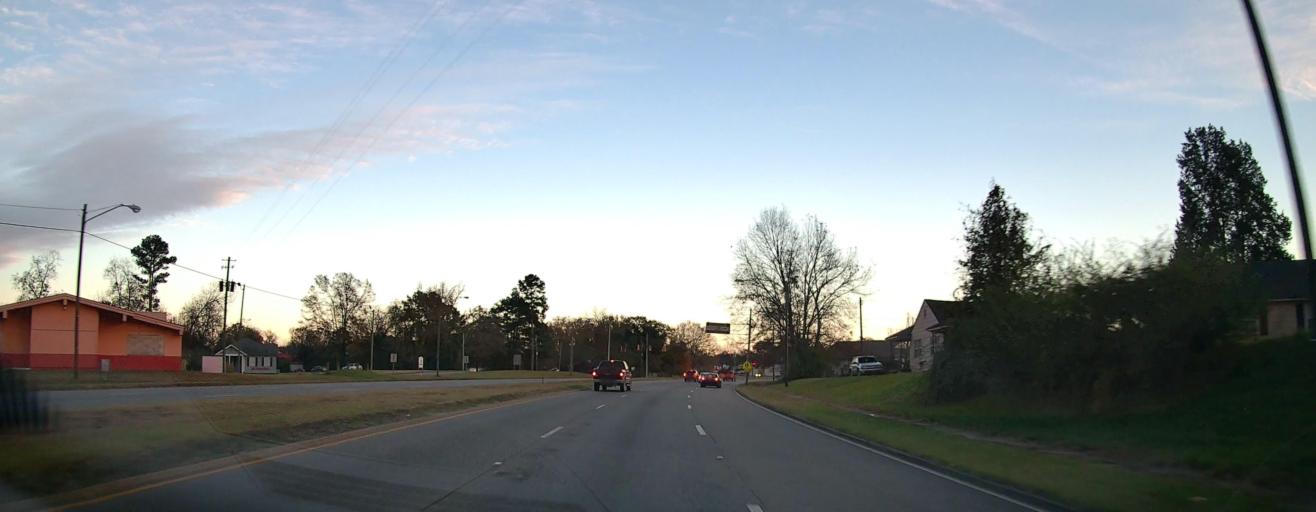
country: US
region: Alabama
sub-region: Etowah County
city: Gadsden
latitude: 34.0055
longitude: -85.9708
